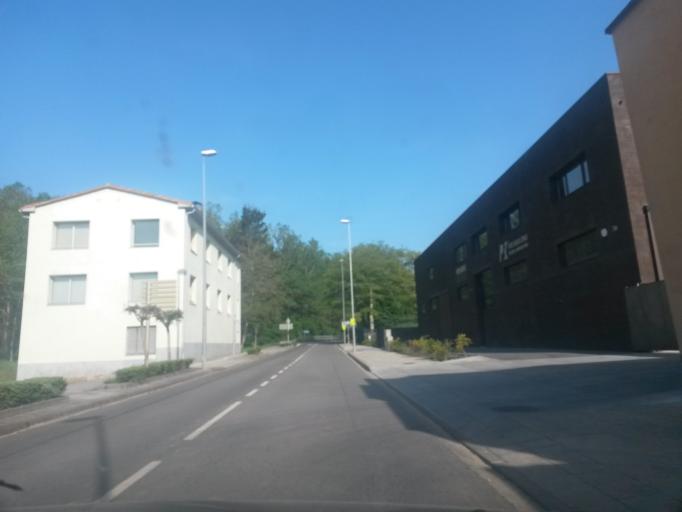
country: ES
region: Catalonia
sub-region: Provincia de Girona
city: Sant Feliu de Pallerols
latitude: 42.0789
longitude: 2.5038
